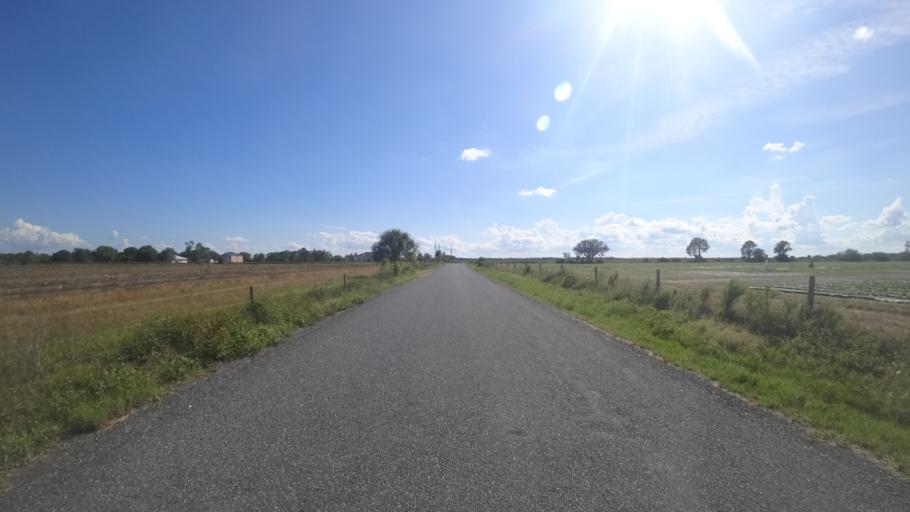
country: US
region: Florida
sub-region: Sarasota County
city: The Meadows
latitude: 27.4320
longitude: -82.2872
